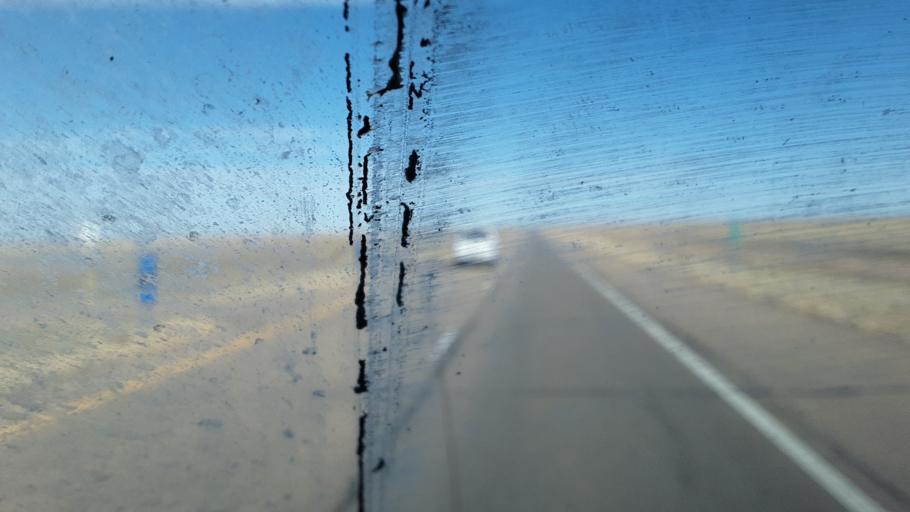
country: US
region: Colorado
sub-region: Weld County
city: Keenesburg
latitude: 40.1731
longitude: -104.3412
